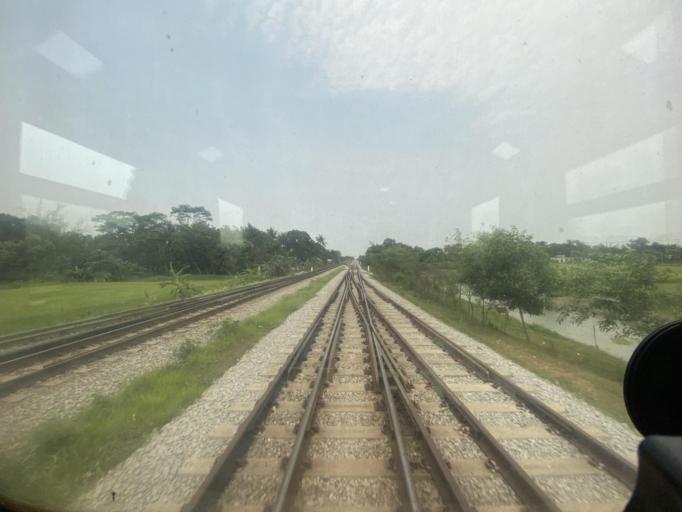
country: BD
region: Chittagong
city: Laksham
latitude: 23.3102
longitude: 91.1395
